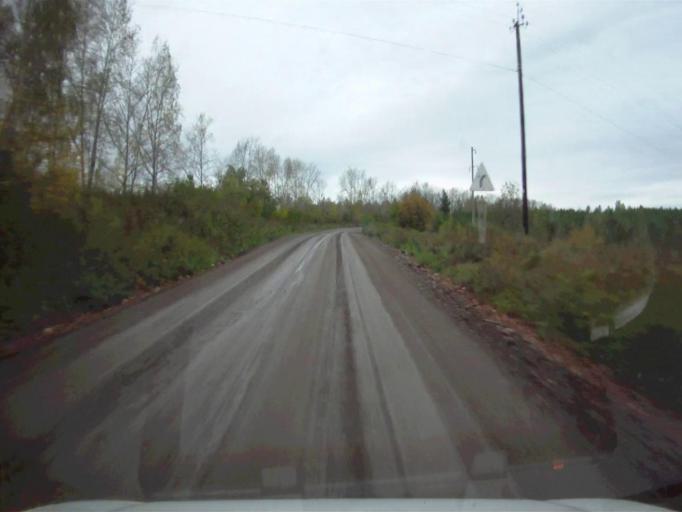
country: RU
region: Chelyabinsk
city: Nyazepetrovsk
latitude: 56.1348
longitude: 59.3064
